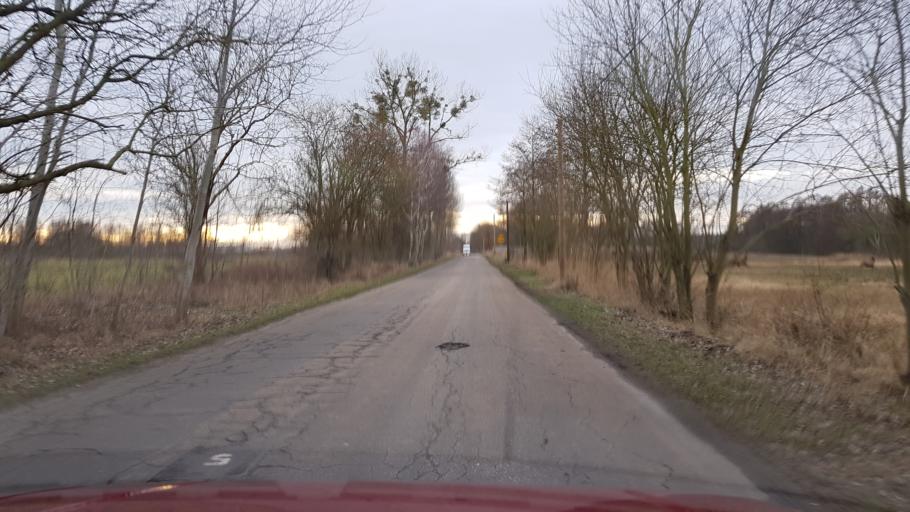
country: PL
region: West Pomeranian Voivodeship
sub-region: Powiat policki
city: Police
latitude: 53.5631
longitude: 14.4958
